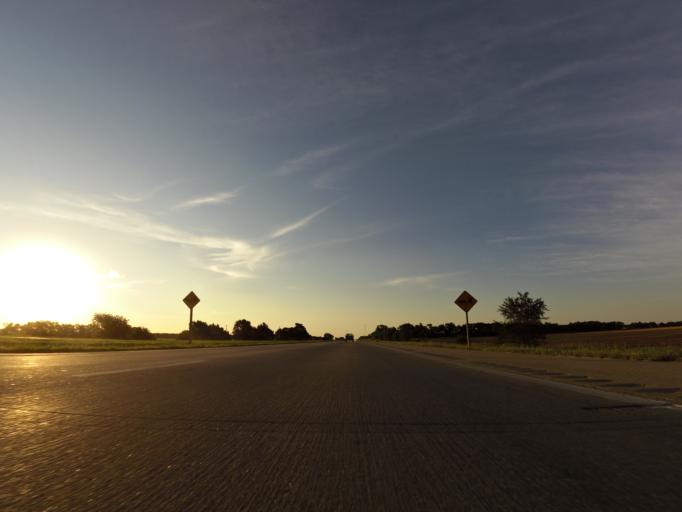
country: US
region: Kansas
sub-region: Reno County
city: Haven
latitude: 37.9215
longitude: -97.8328
